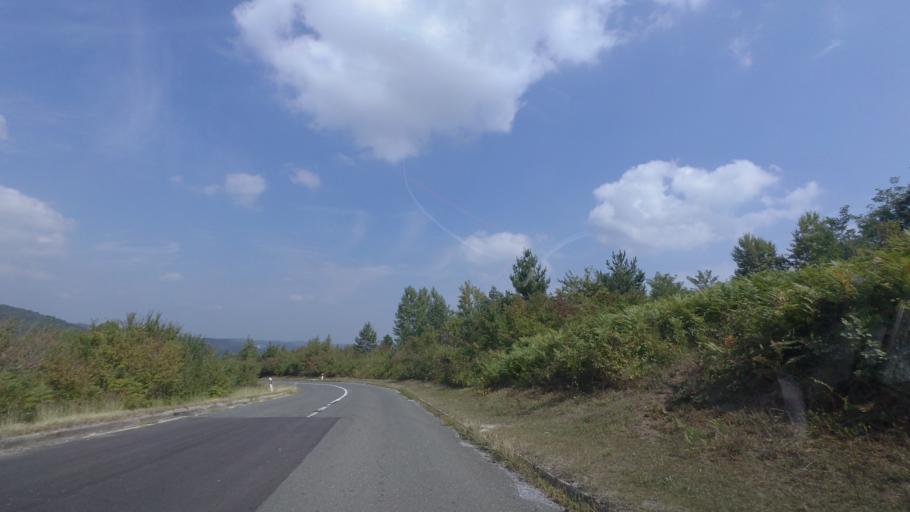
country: BA
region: Federation of Bosnia and Herzegovina
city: Zboriste
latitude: 45.1628
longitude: 16.1389
